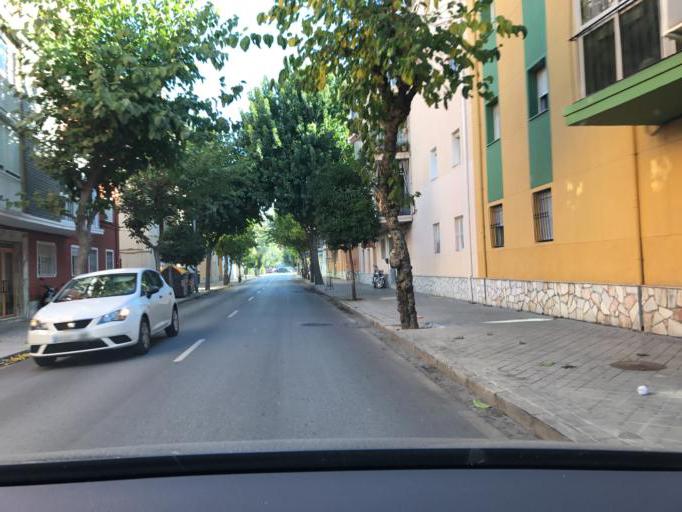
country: ES
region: Andalusia
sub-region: Provincia de Granada
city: Granada
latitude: 37.1631
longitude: -3.5983
